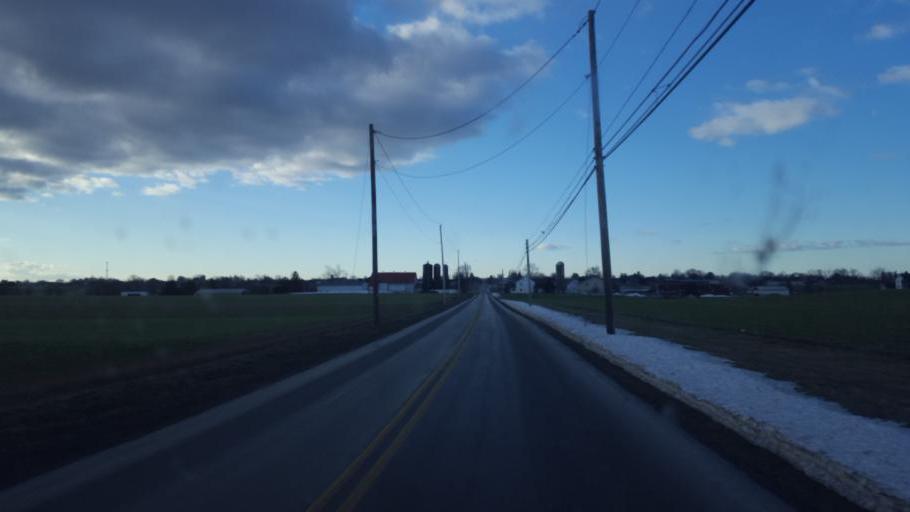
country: US
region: Pennsylvania
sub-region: Lancaster County
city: Intercourse
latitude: 40.0491
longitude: -76.1037
